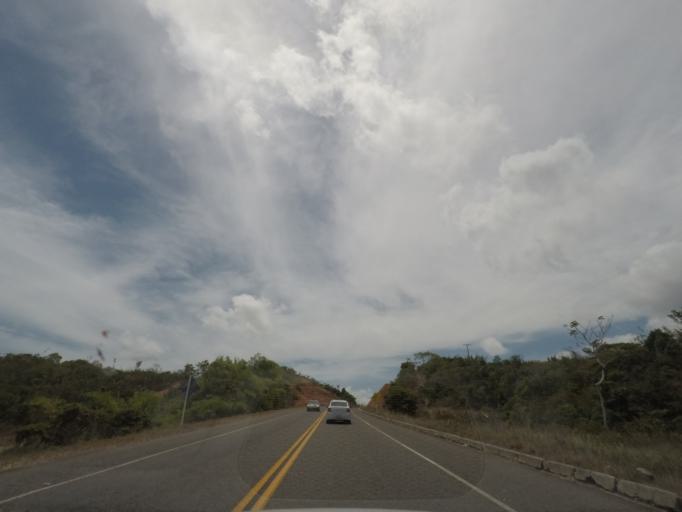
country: BR
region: Bahia
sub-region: Conde
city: Conde
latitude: -11.9098
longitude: -37.6571
